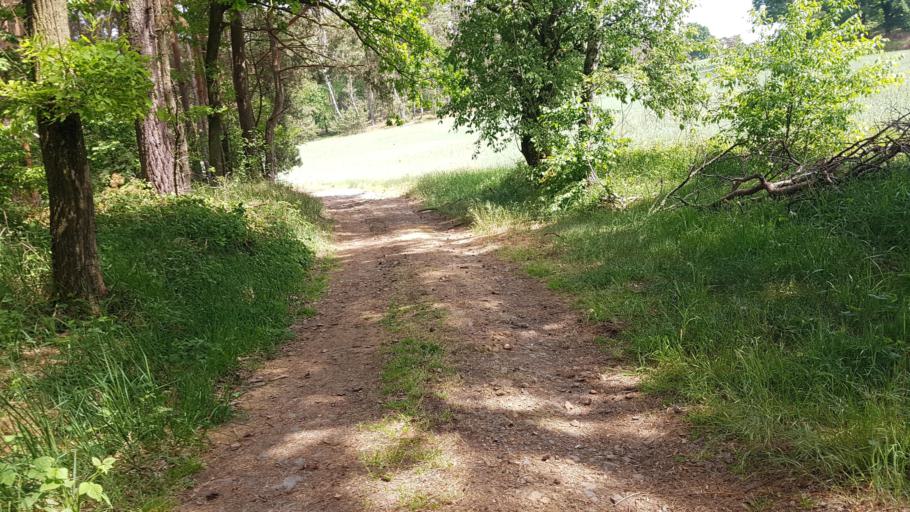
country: DE
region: Brandenburg
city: Grosskmehlen
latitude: 51.3727
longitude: 13.7033
